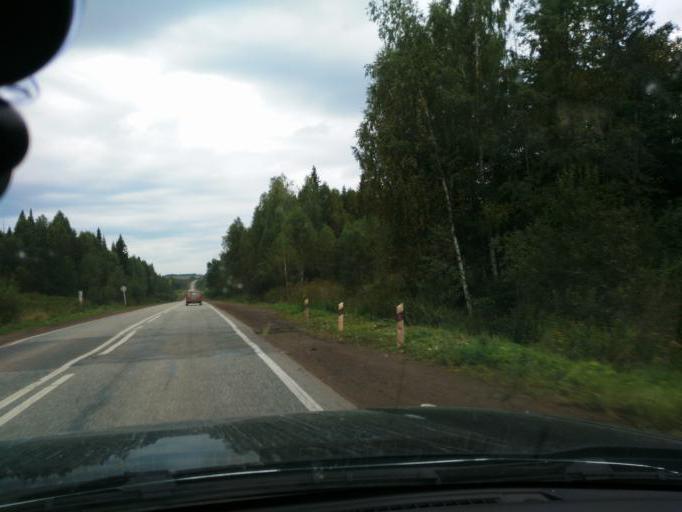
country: RU
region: Perm
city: Chernushka
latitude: 56.8016
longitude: 56.0679
